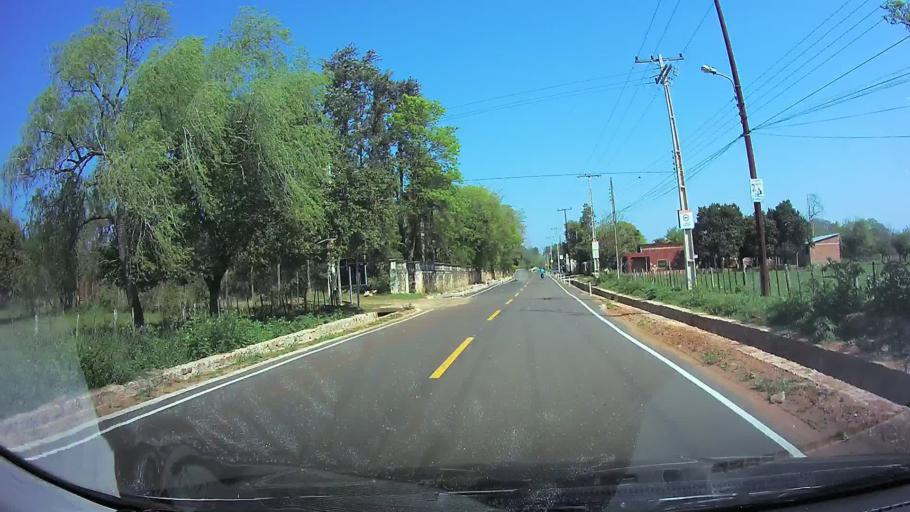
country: PY
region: Central
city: Limpio
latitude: -25.2318
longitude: -57.4908
